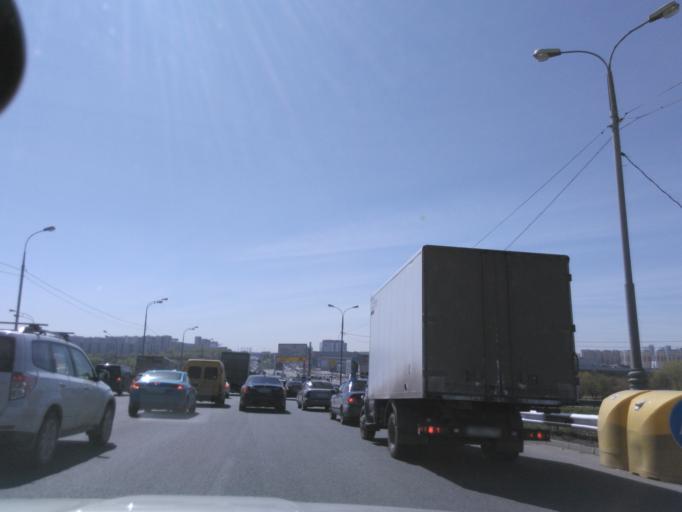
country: RU
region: Moscow
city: Strogino
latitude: 55.8320
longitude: 37.3951
